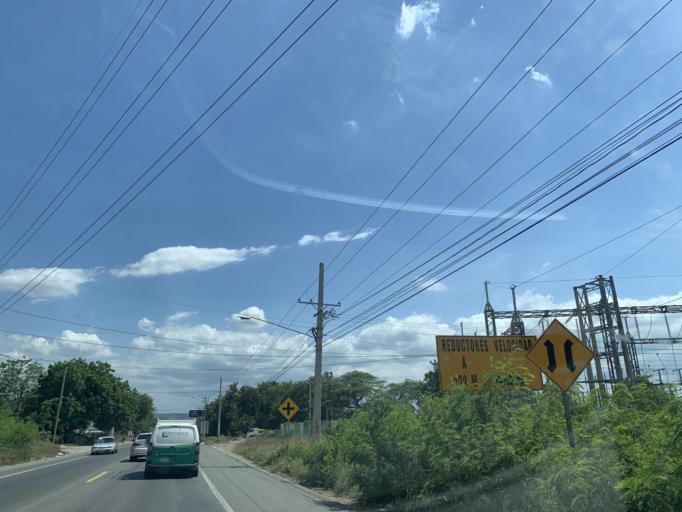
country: DO
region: Santiago
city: Villa Bisono
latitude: 19.5604
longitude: -70.8589
